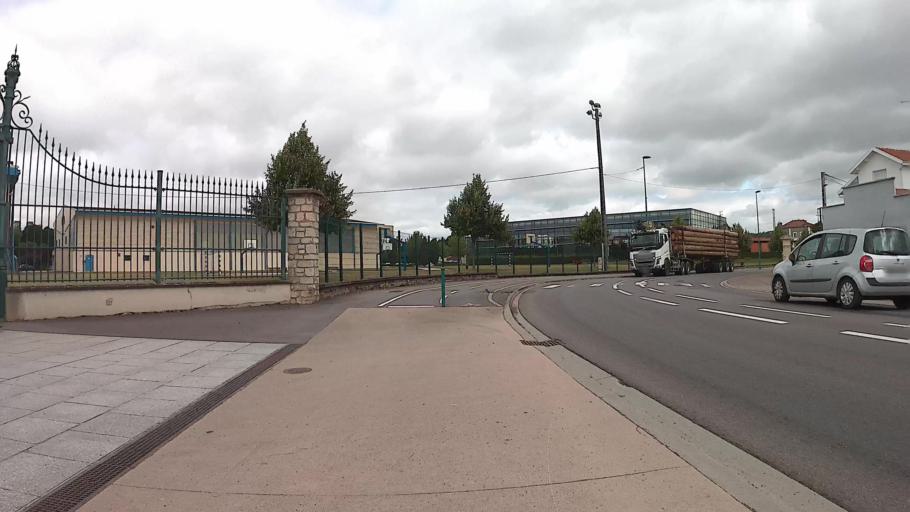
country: FR
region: Lorraine
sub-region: Departement de la Meuse
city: Verdun
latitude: 49.1594
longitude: 5.3934
